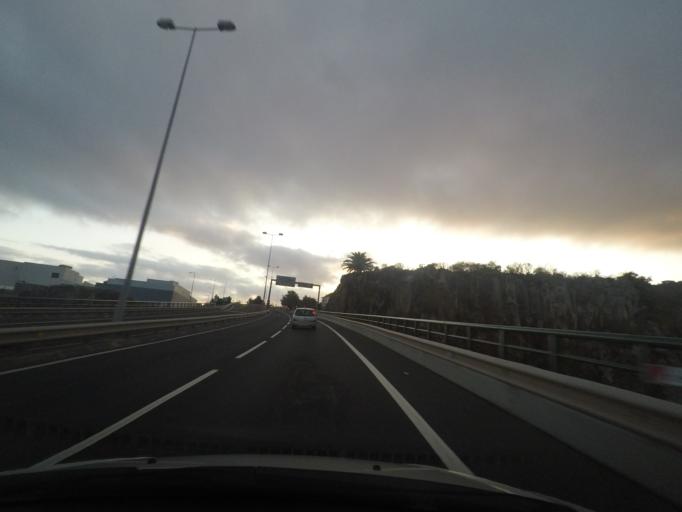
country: PT
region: Madeira
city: Canico
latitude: 32.6494
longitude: -16.8330
